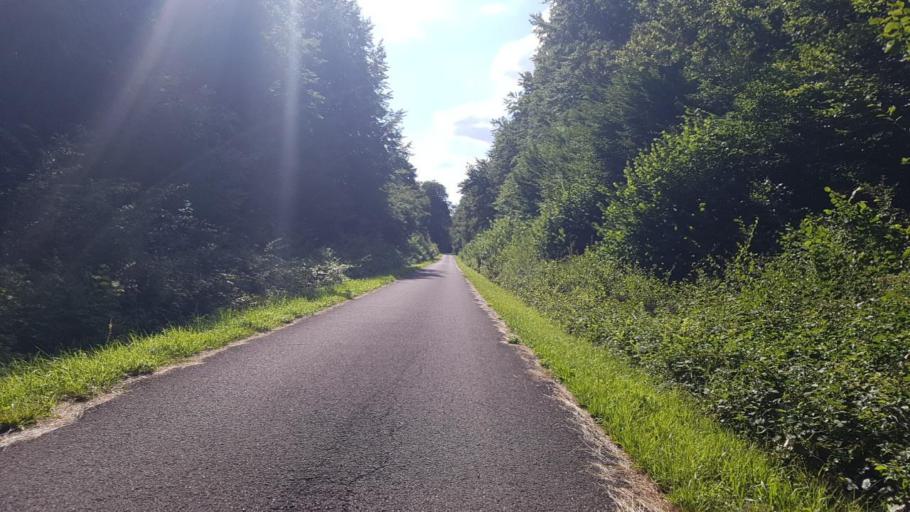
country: FR
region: Picardie
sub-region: Departement de l'Oise
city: Ver-sur-Launette
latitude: 49.1138
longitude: 2.6591
